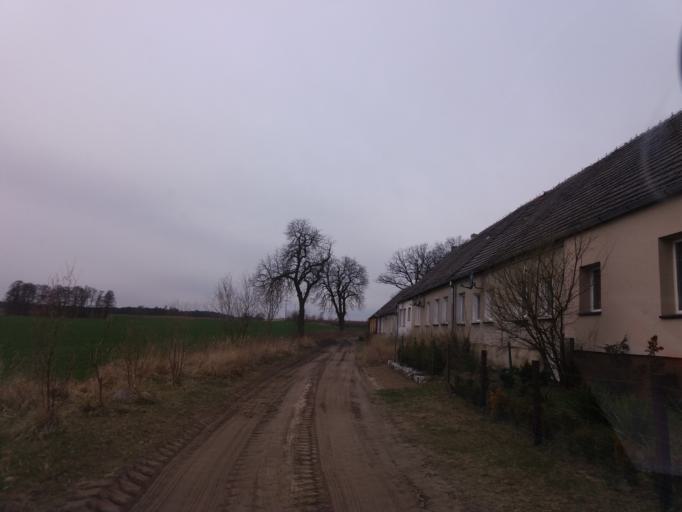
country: PL
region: West Pomeranian Voivodeship
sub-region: Powiat choszczenski
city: Recz
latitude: 53.1575
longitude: 15.6123
